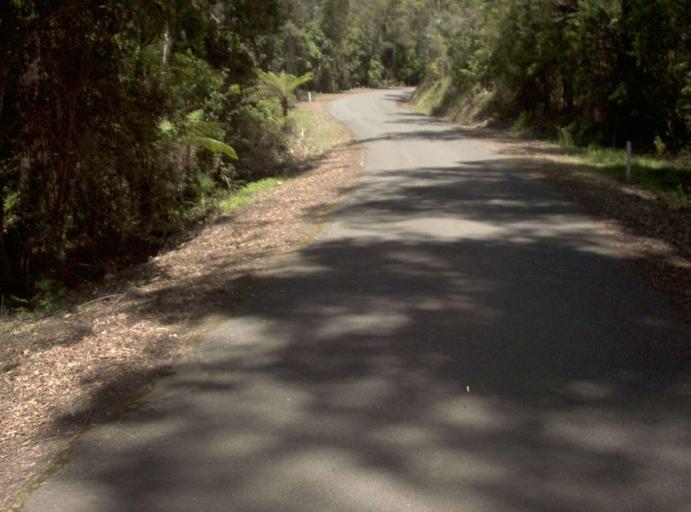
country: AU
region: New South Wales
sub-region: Bombala
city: Bombala
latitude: -37.4939
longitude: 148.9253
